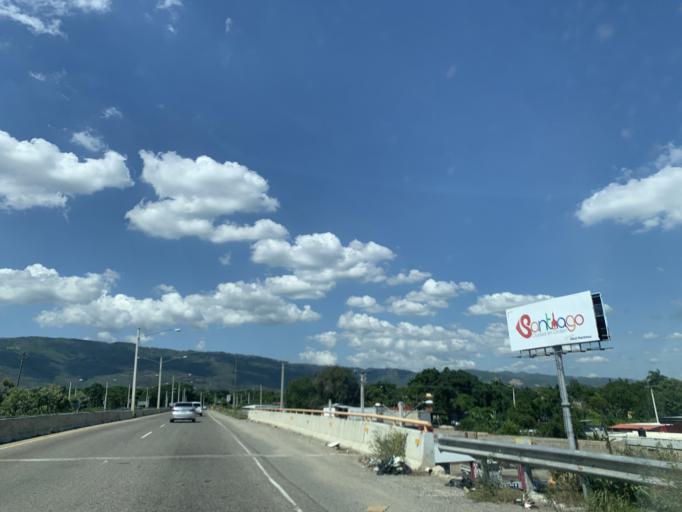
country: DO
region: Santiago
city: Palmar Arriba
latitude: 19.5171
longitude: -70.7637
